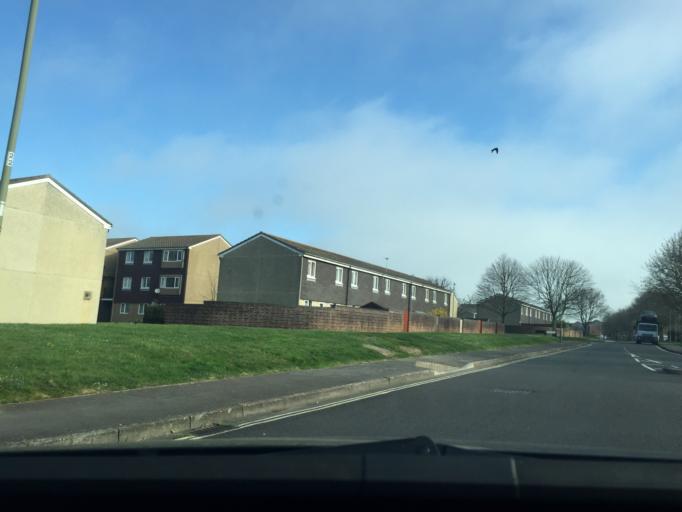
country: GB
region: England
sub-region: Hampshire
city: Gosport
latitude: 50.8071
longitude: -1.1363
